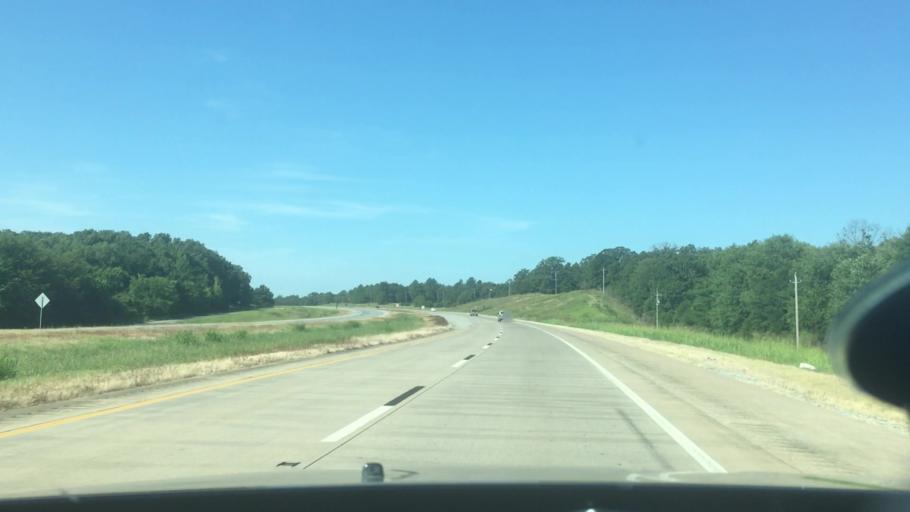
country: US
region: Oklahoma
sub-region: Atoka County
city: Atoka
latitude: 34.2999
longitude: -96.1870
